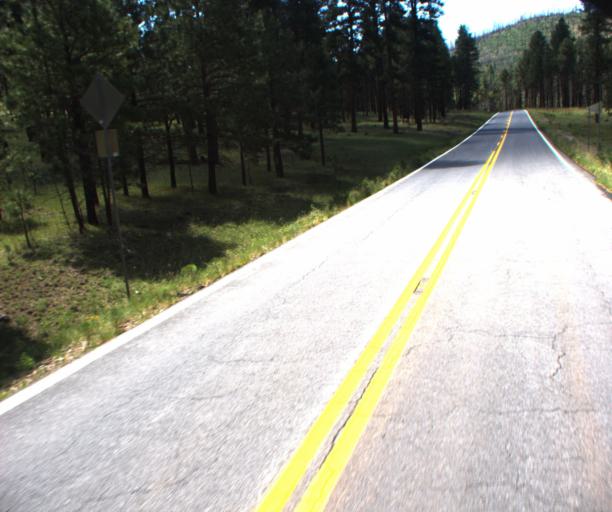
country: US
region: Arizona
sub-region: Apache County
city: Eagar
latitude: 33.7547
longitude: -109.2167
